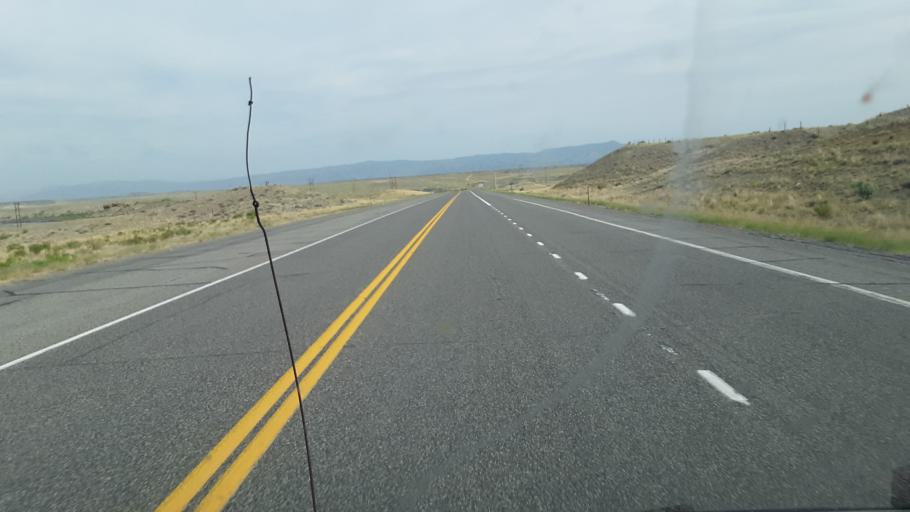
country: US
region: Wyoming
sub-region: Fremont County
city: Riverton
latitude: 43.2777
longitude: -108.1207
